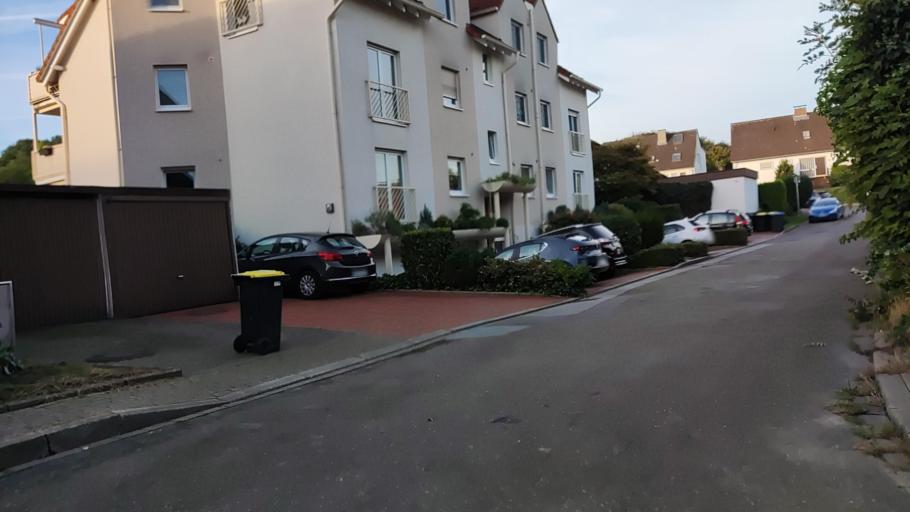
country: DE
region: North Rhine-Westphalia
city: Castrop-Rauxel
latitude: 51.5413
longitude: 7.2877
